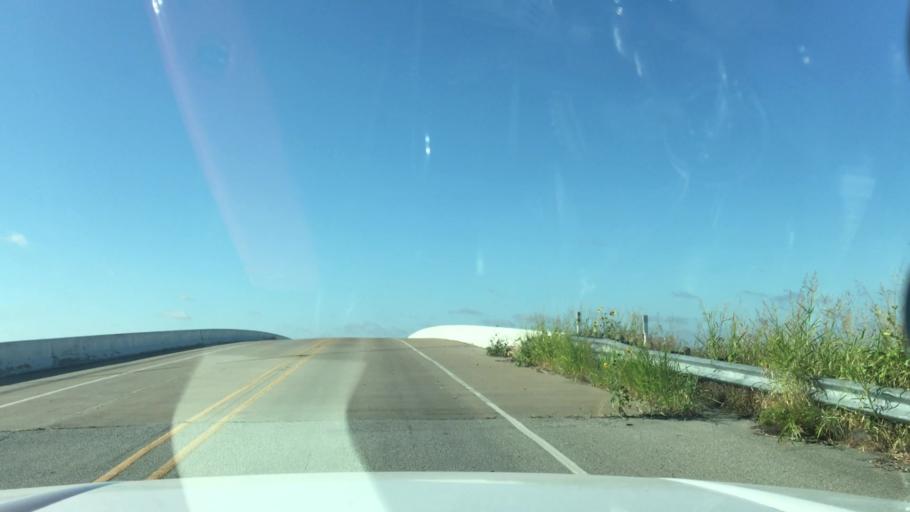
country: US
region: Texas
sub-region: Ellis County
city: Nash
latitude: 32.2607
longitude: -96.8733
